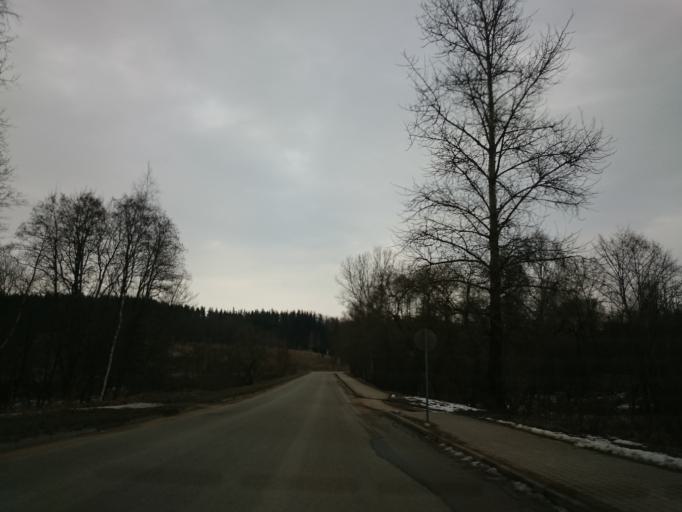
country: LV
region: Cesu Rajons
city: Cesis
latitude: 57.3213
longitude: 25.2566
